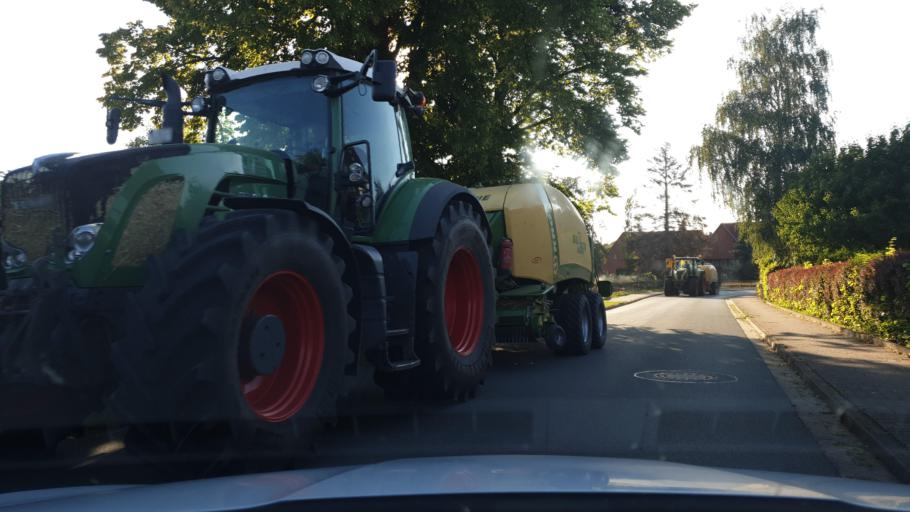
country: DE
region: Lower Saxony
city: Nienstadt
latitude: 52.2916
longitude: 9.1692
